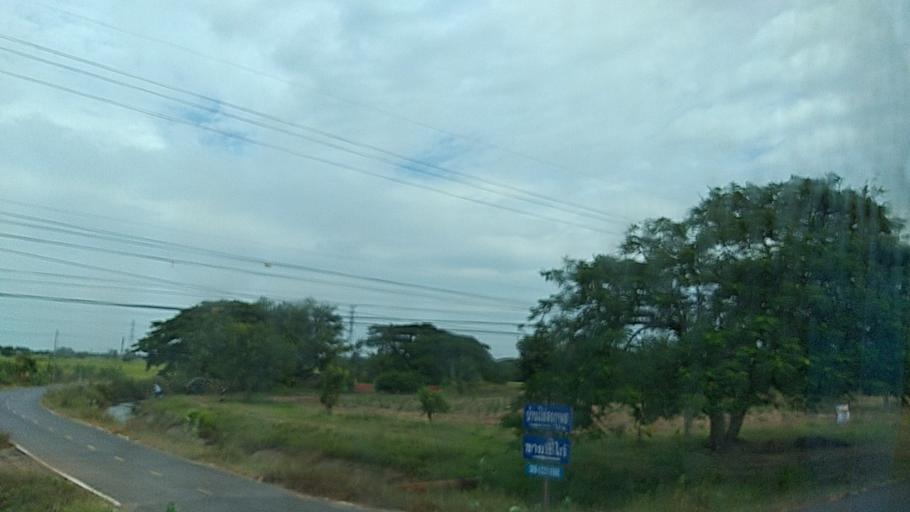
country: TH
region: Roi Et
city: Changhan
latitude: 16.1232
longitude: 103.4797
